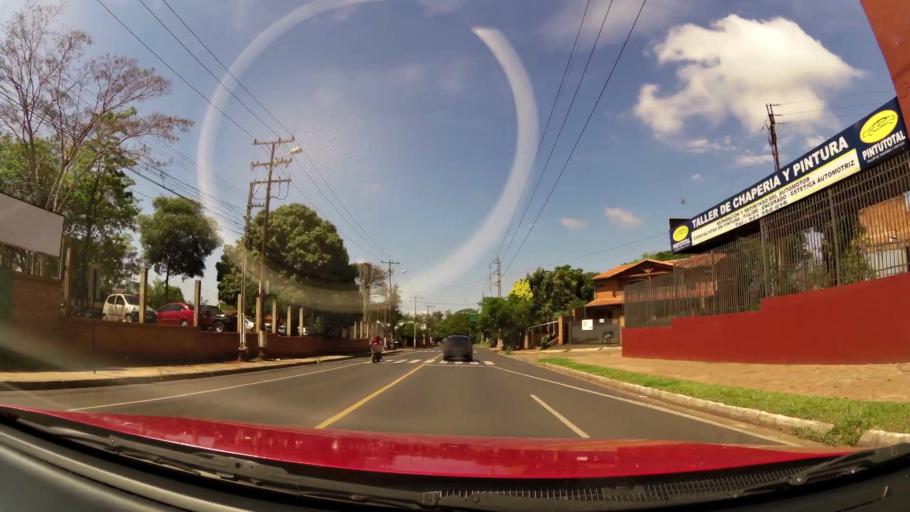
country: PY
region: Central
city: San Lorenzo
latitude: -25.3328
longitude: -57.5104
